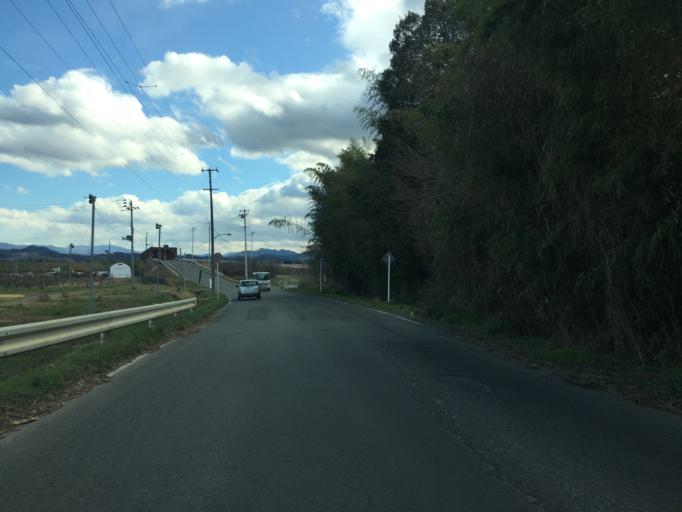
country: JP
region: Fukushima
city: Yanagawamachi-saiwaicho
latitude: 37.8659
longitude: 140.5681
